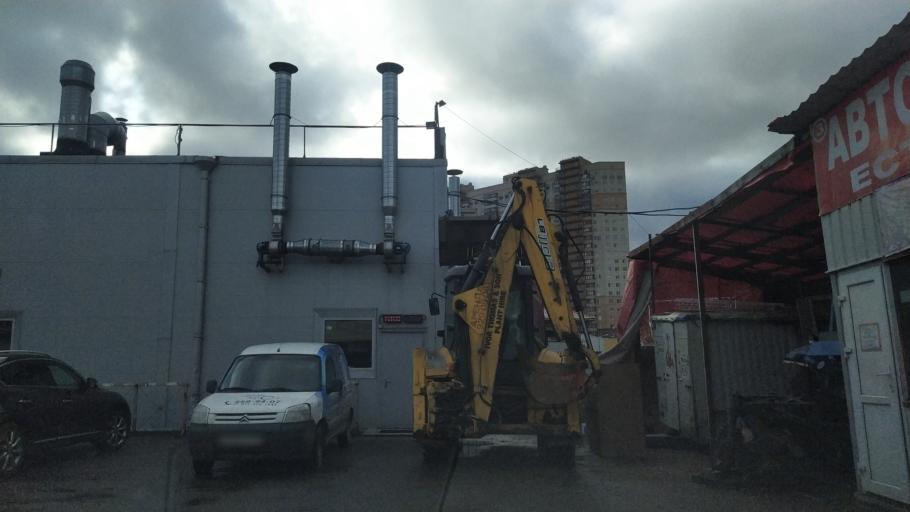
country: RU
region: St.-Petersburg
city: Grazhdanka
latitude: 60.0352
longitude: 30.4071
